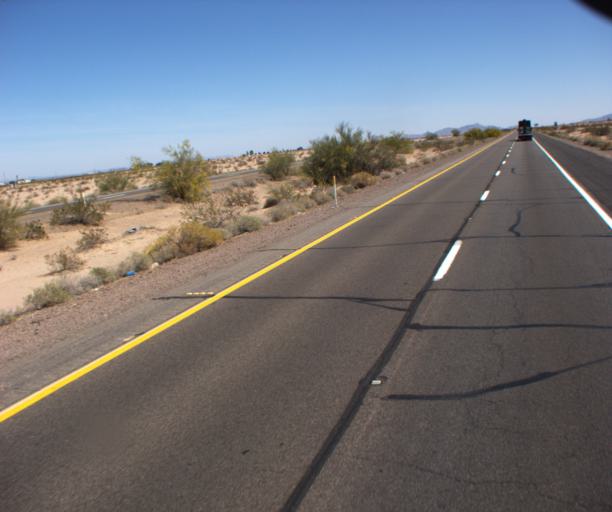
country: US
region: Arizona
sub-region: Yuma County
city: Wellton
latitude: 32.6830
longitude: -114.0143
